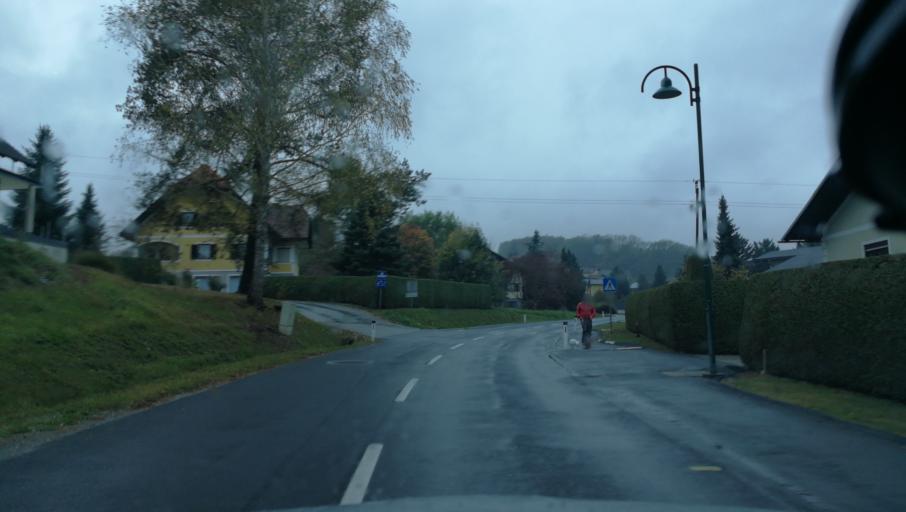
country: AT
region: Styria
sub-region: Politischer Bezirk Leibnitz
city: Spielfeld
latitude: 46.7046
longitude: 15.6275
